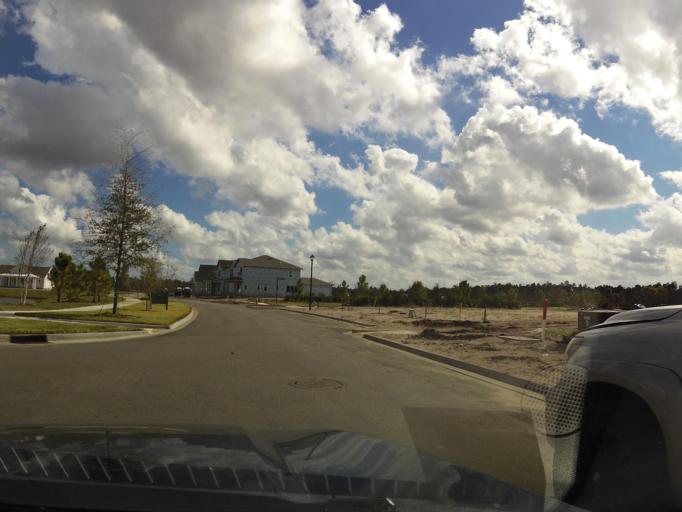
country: US
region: Florida
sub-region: Saint Johns County
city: Ponte Vedra Beach
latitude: 30.2464
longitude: -81.4969
